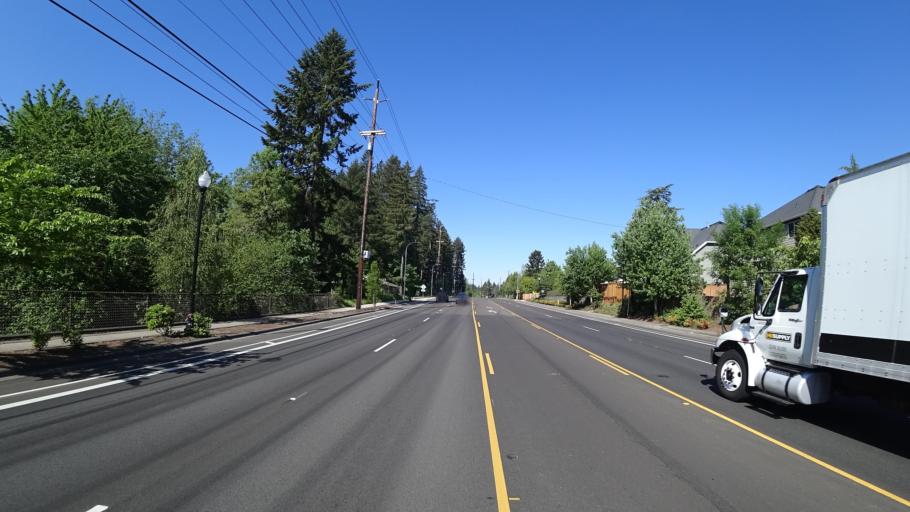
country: US
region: Oregon
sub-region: Washington County
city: Rockcreek
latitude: 45.5202
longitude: -122.9161
